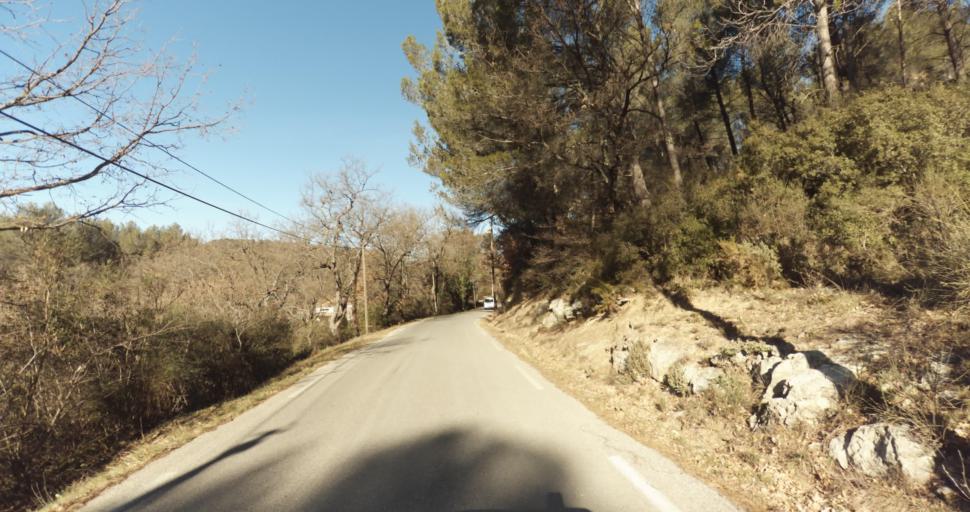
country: FR
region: Provence-Alpes-Cote d'Azur
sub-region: Departement des Bouches-du-Rhone
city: Peypin
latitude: 43.3653
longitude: 5.5669
